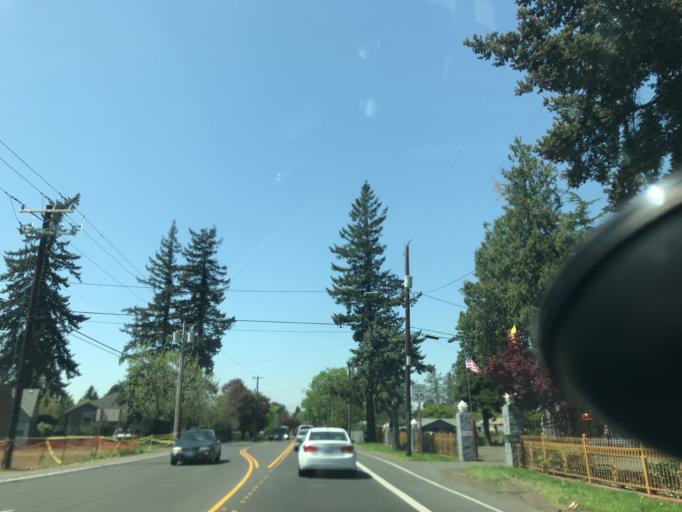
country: US
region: Oregon
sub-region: Clackamas County
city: Happy Valley
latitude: 45.4983
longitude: -122.5113
